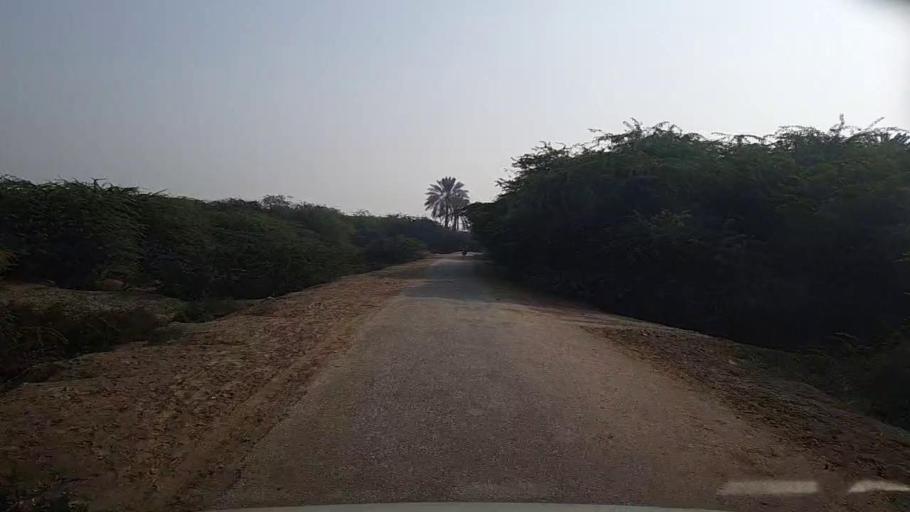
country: PK
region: Sindh
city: Kandiari
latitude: 27.0492
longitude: 68.4619
